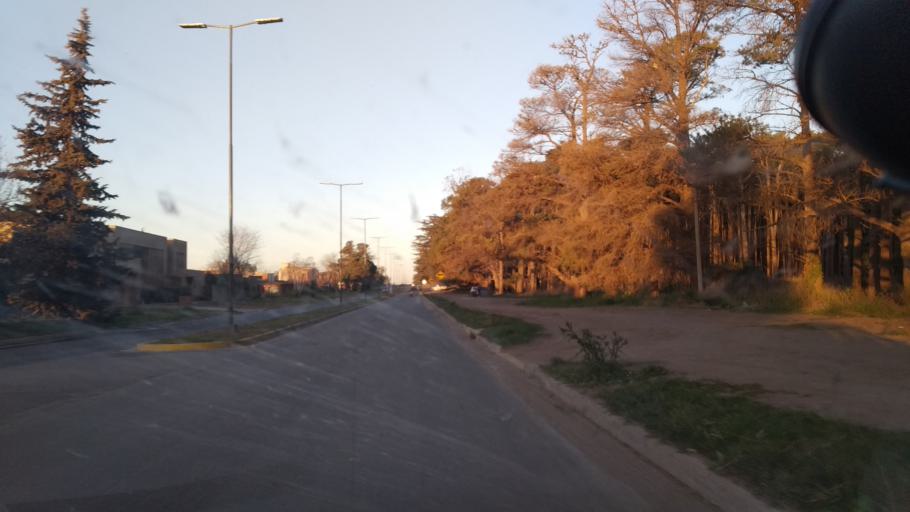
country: AR
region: Buenos Aires
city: Necochea
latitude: -38.5853
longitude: -58.7499
